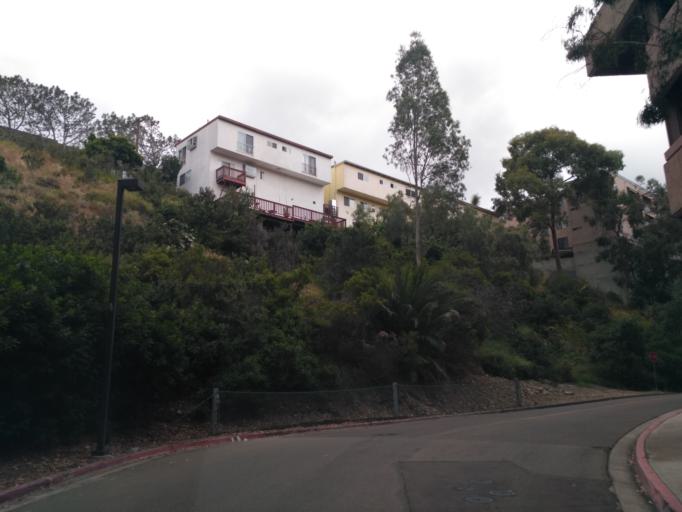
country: US
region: California
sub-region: San Diego County
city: San Diego
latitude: 32.7557
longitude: -117.1631
